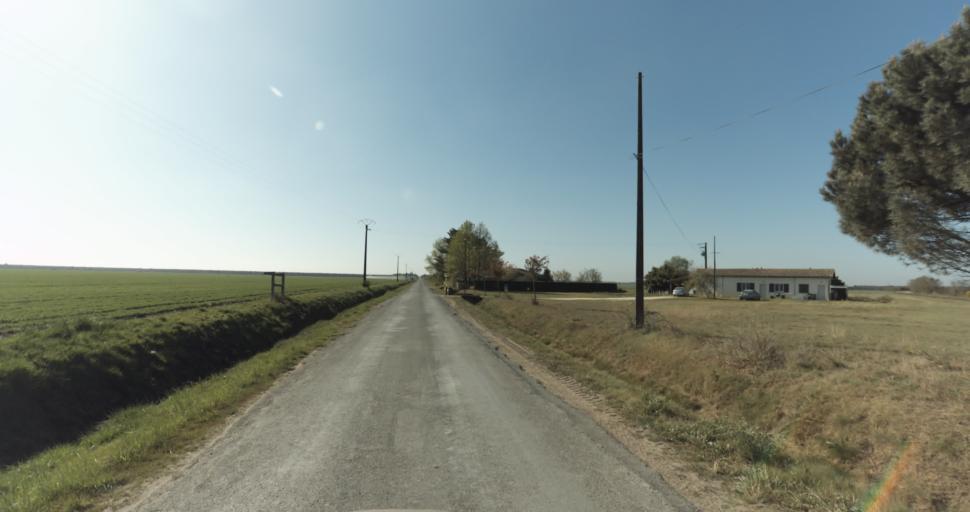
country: FR
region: Aquitaine
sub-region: Departement de la Gironde
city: Marcheprime
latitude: 44.7751
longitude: -0.8586
